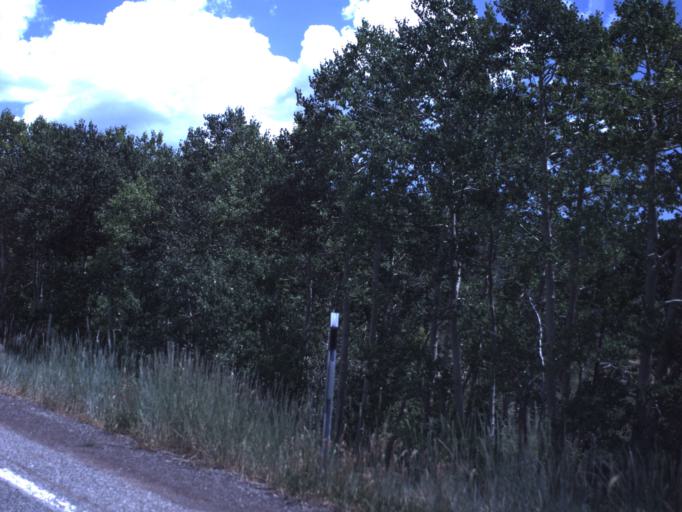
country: US
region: Utah
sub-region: Sanpete County
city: Fairview
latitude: 39.6749
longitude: -111.3096
